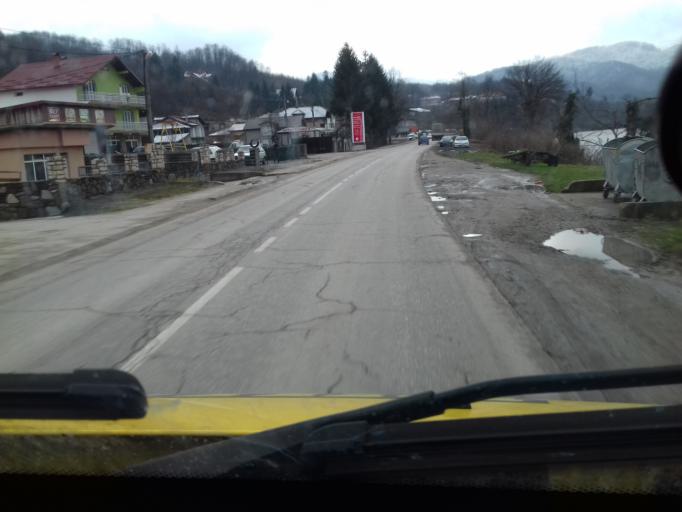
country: BA
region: Federation of Bosnia and Herzegovina
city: Dubravica
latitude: 44.4218
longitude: 18.1320
